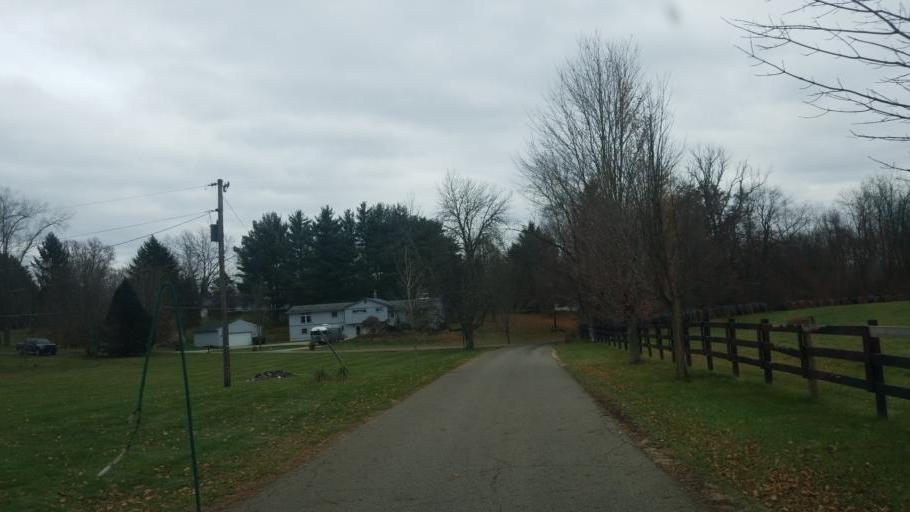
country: US
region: Ohio
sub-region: Knox County
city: Fredericktown
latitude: 40.5008
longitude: -82.5277
